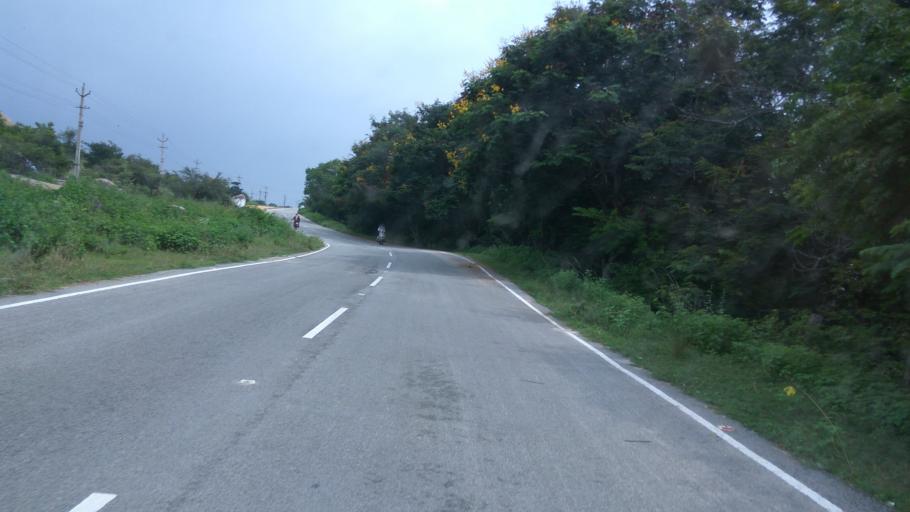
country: IN
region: Telangana
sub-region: Rangareddi
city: Ghatkesar
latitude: 17.5381
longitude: 78.6920
